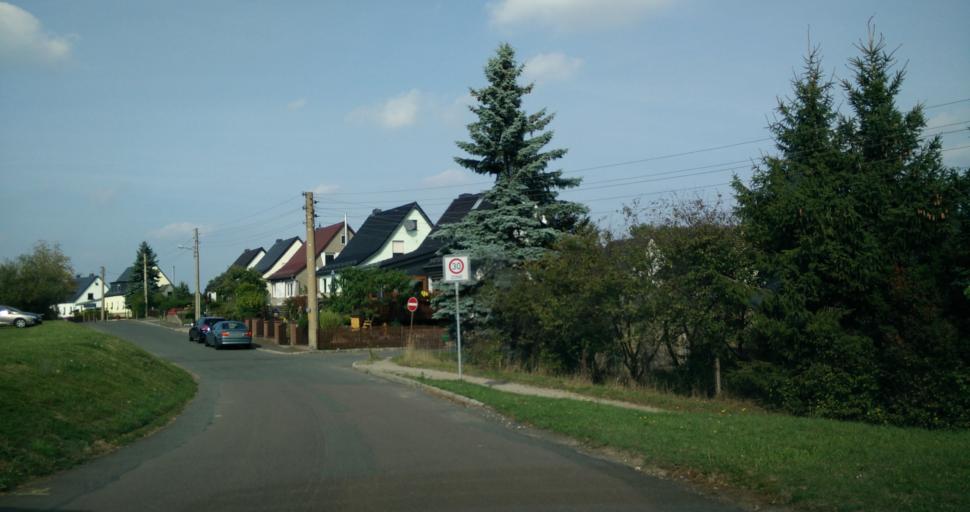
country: DE
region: Saxony
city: Colditz
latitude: 51.1361
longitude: 12.7950
